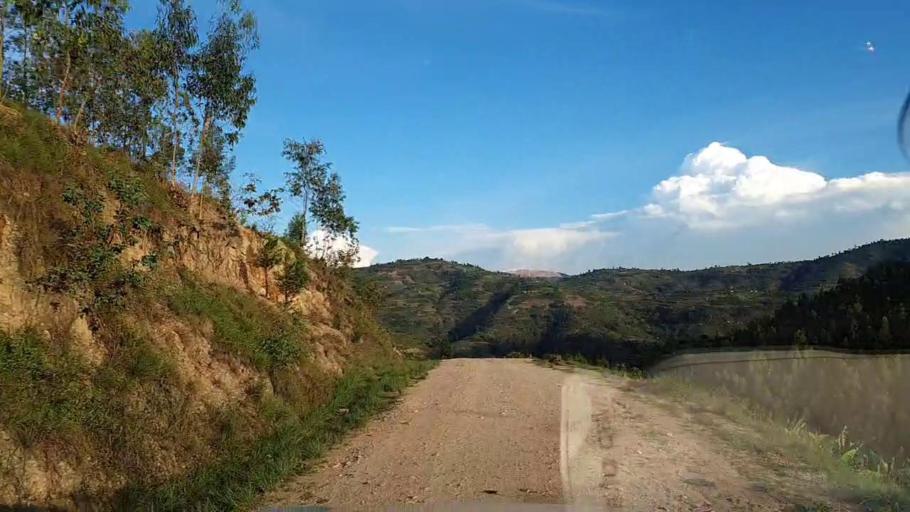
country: RW
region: Southern Province
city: Gikongoro
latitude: -2.3976
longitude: 29.5576
